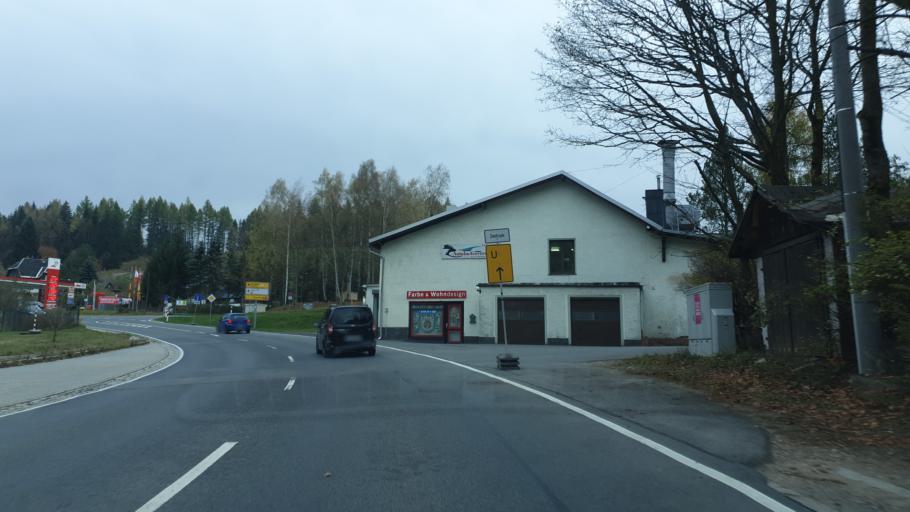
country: DE
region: Saxony
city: Johanngeorgenstadt
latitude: 50.4456
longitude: 12.7275
